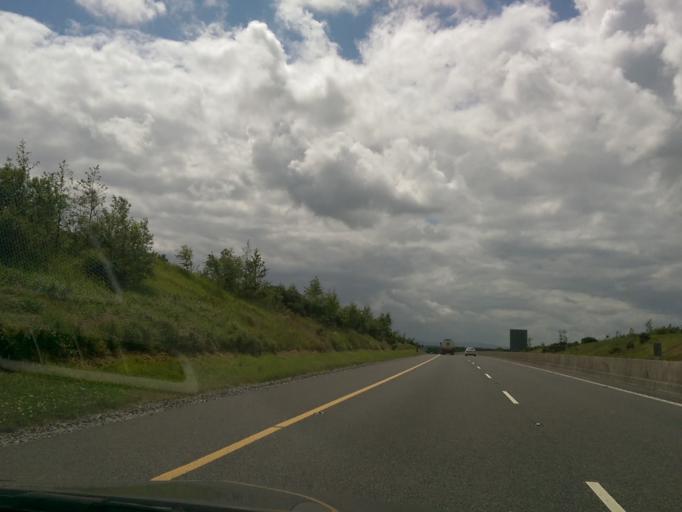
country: IE
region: Munster
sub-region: County Cork
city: Mitchelstown
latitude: 52.2800
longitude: -8.2263
